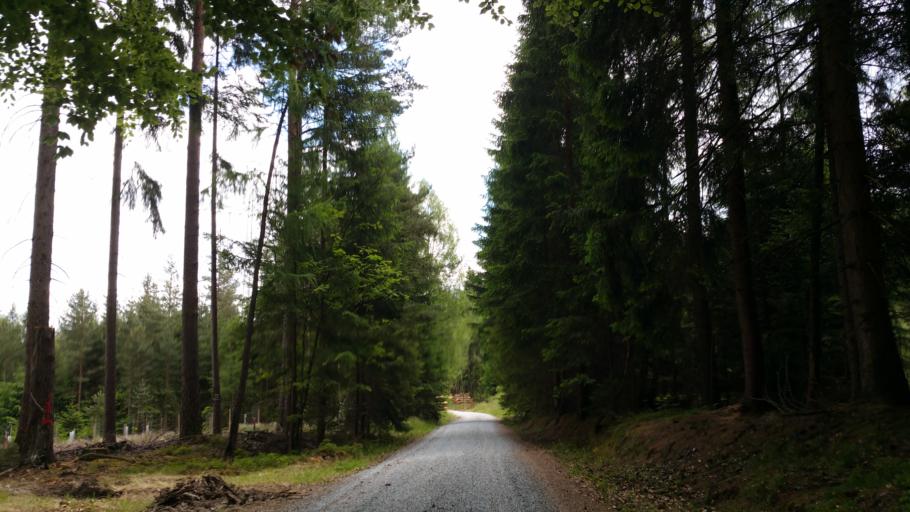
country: DE
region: Bavaria
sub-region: Upper Franconia
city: Kirchenlamitz
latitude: 50.1702
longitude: 11.9327
